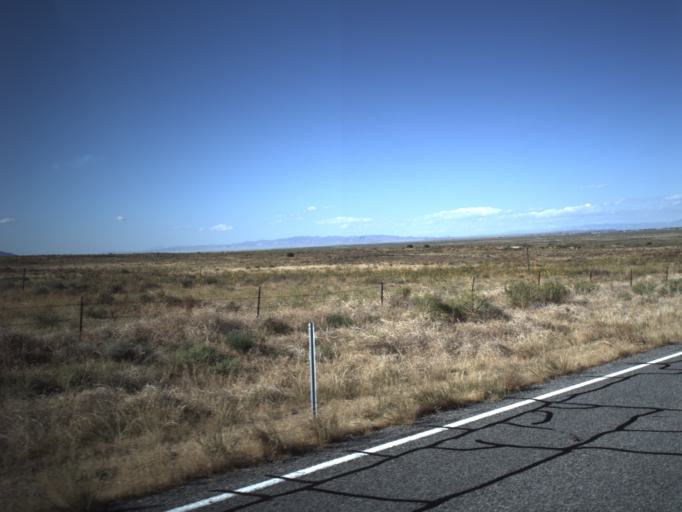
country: US
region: Utah
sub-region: Millard County
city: Delta
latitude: 39.3548
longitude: -112.3782
